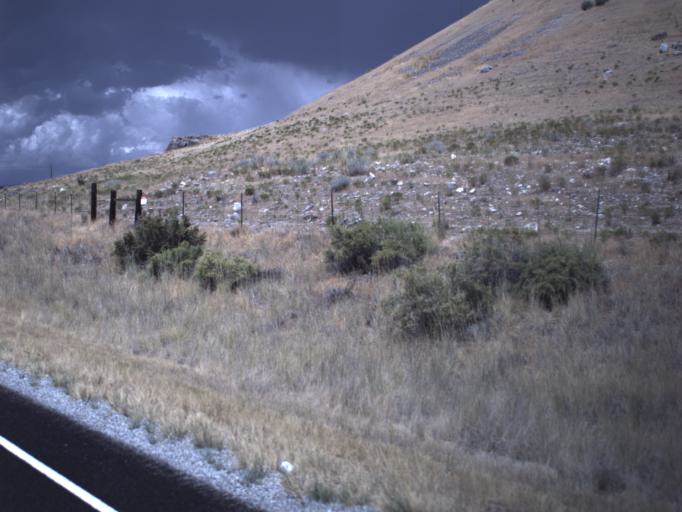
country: US
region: Utah
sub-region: Box Elder County
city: Tremonton
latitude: 41.6150
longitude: -112.3775
